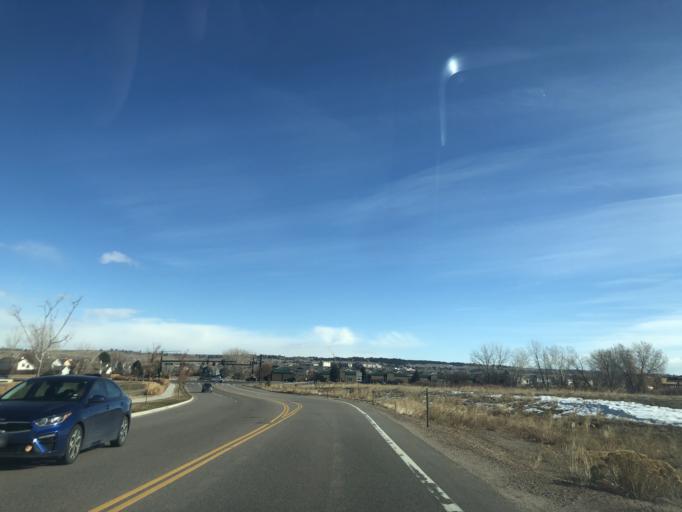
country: US
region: Colorado
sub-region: Douglas County
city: Stonegate
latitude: 39.5540
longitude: -104.7970
